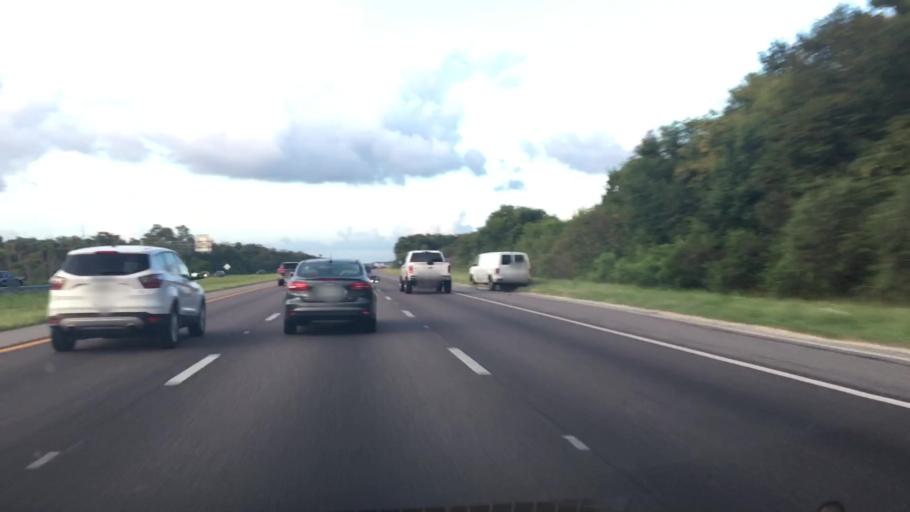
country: US
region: Florida
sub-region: Volusia County
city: DeBary
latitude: 28.8432
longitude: -81.3122
